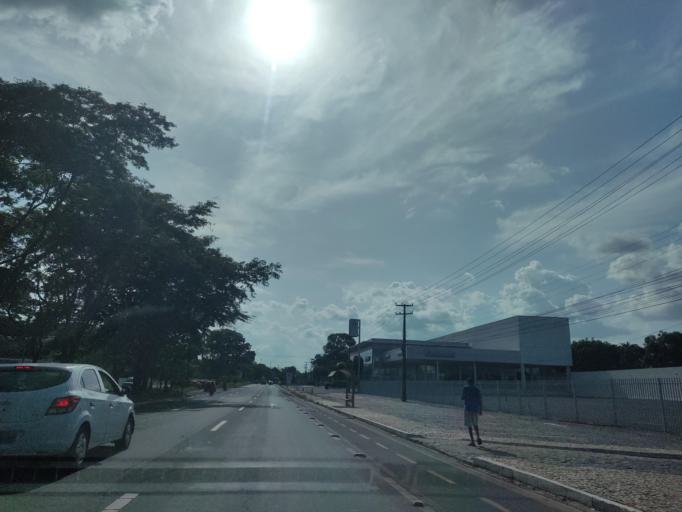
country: BR
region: Piaui
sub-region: Teresina
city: Teresina
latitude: -5.0813
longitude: -42.7667
